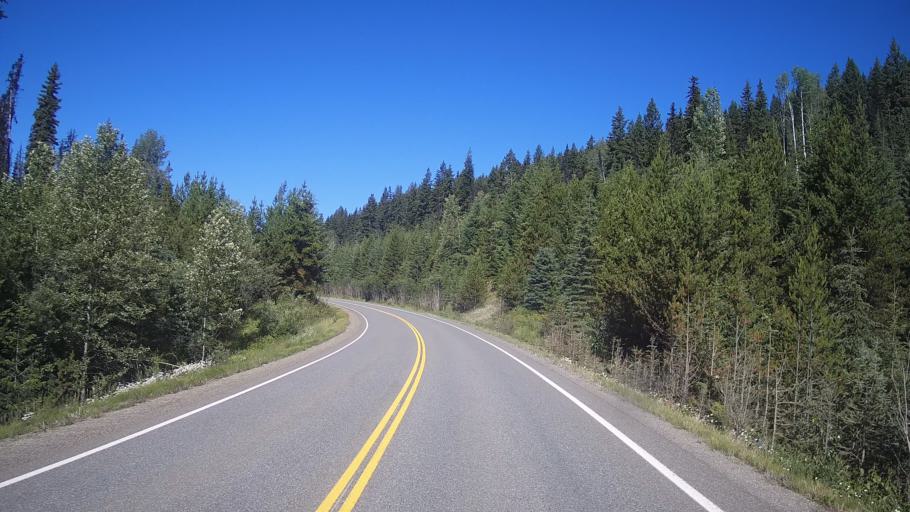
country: CA
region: British Columbia
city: Kamloops
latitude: 51.4966
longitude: -120.4199
